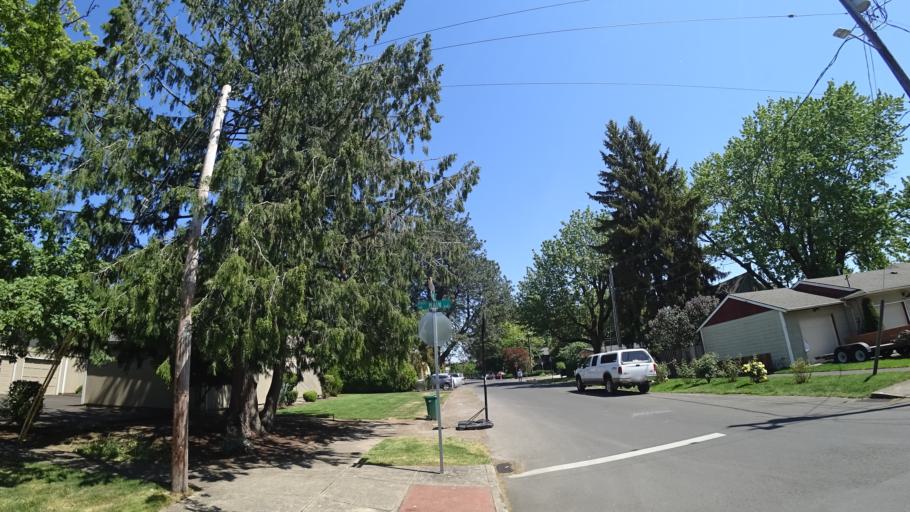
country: US
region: Oregon
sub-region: Washington County
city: Beaverton
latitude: 45.4845
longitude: -122.8087
